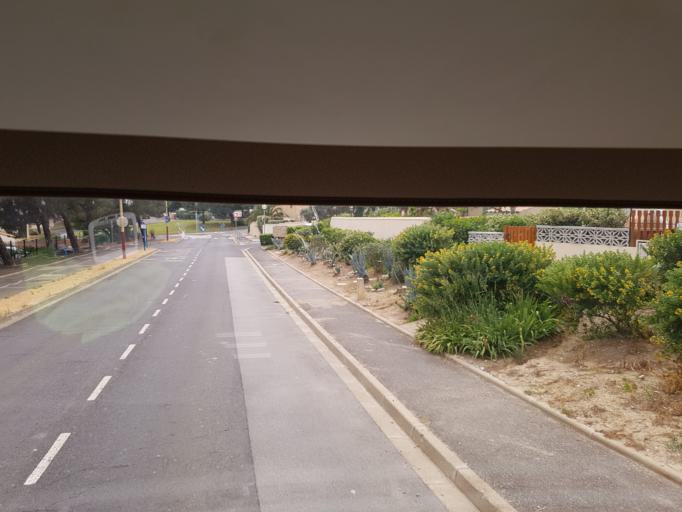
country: FR
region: Languedoc-Roussillon
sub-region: Departement de l'Aude
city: Fleury
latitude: 43.1824
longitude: 3.1857
